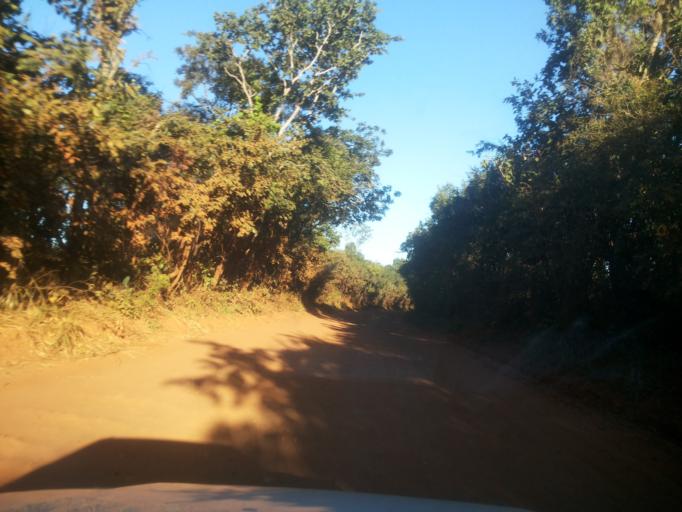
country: BR
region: Minas Gerais
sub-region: Campina Verde
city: Campina Verde
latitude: -19.3273
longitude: -49.7774
